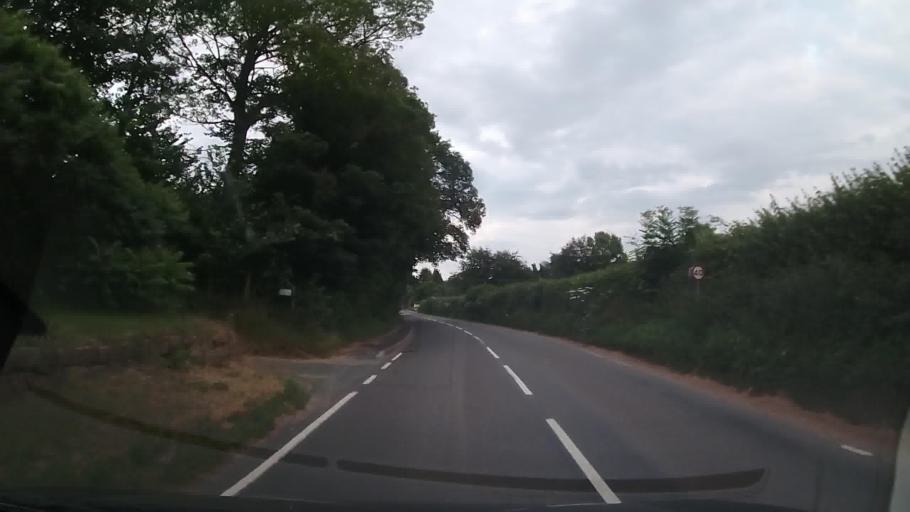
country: GB
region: England
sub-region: Shropshire
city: Great Ness
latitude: 52.7951
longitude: -2.9087
